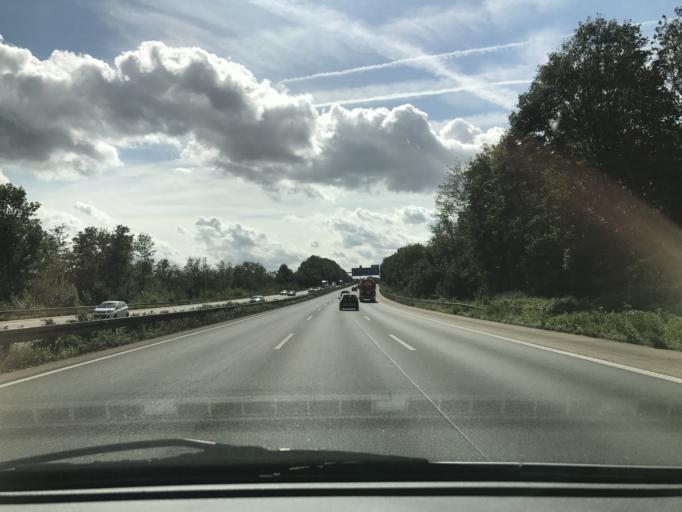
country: DE
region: North Rhine-Westphalia
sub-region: Regierungsbezirk Dusseldorf
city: Ratingen
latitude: 51.3118
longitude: 6.8989
